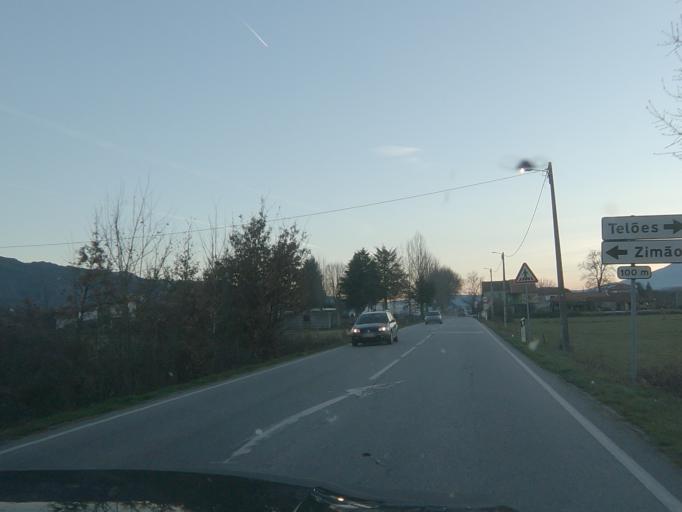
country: PT
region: Vila Real
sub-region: Vila Pouca de Aguiar
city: Vila Pouca de Aguiar
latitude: 41.4522
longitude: -7.6689
